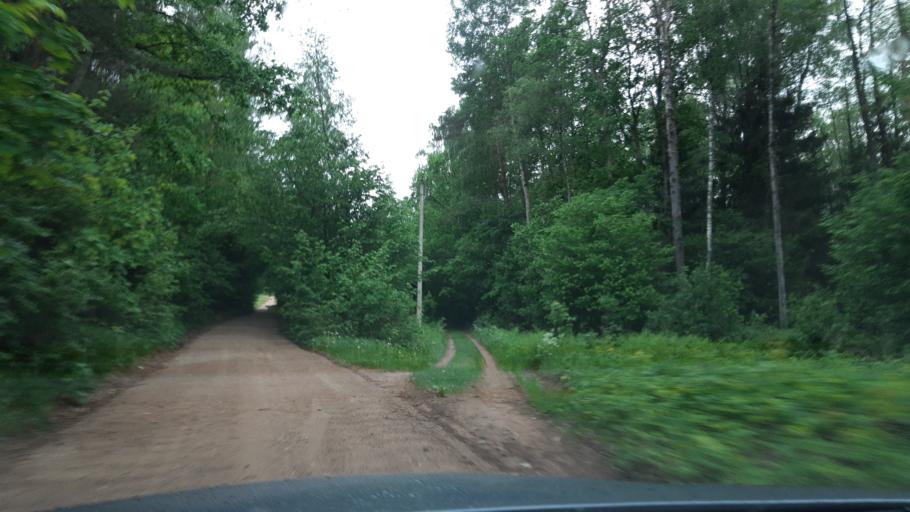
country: LT
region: Utenos apskritis
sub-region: Anyksciai
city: Anyksciai
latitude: 55.4501
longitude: 25.2108
